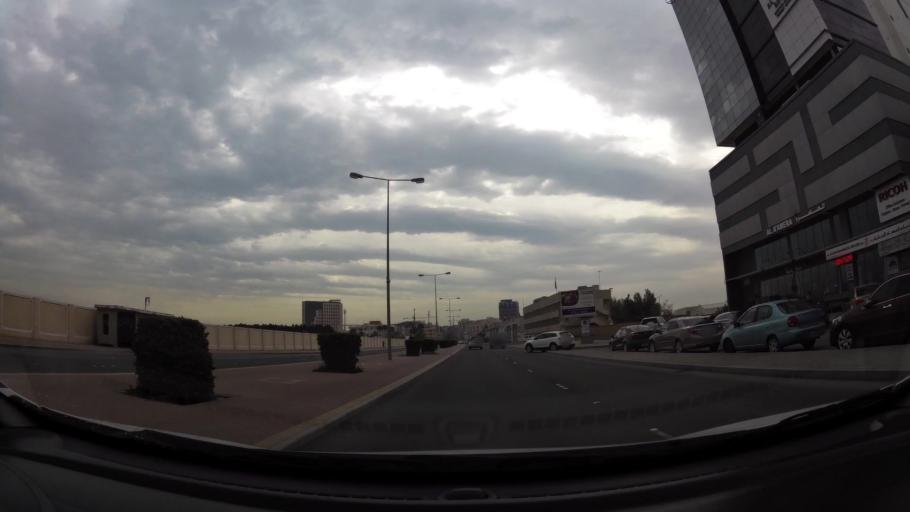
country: BH
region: Manama
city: Manama
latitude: 26.2097
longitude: 50.5935
